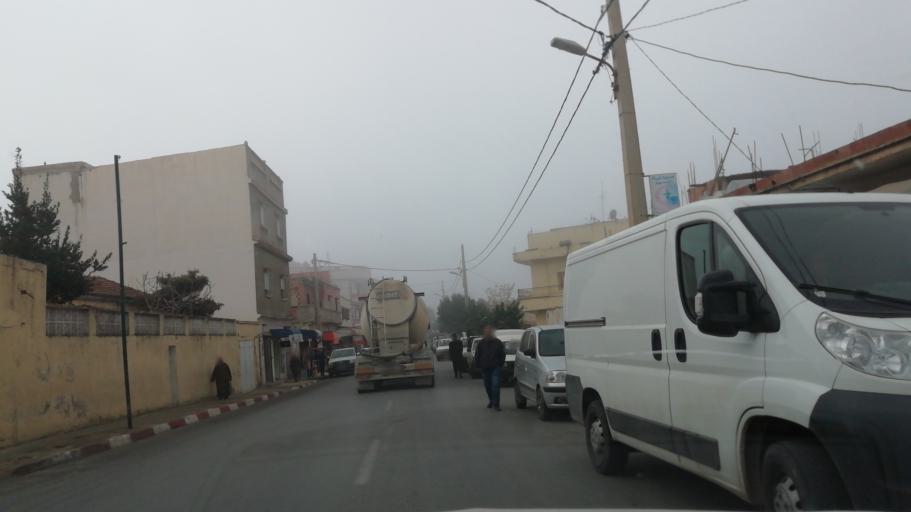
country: DZ
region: Mascara
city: Mascara
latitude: 35.5174
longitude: 0.3050
